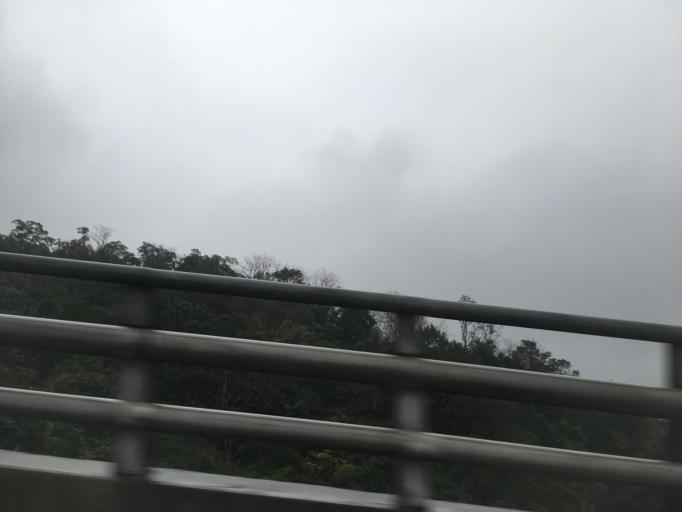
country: TW
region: Taiwan
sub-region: Keelung
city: Keelung
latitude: 25.0472
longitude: 121.7785
